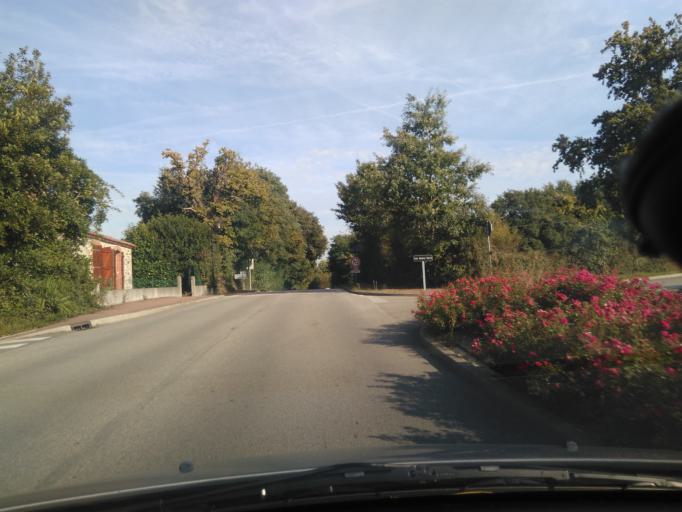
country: FR
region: Pays de la Loire
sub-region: Departement de la Vendee
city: Aubigny
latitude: 46.5943
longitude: -1.4480
